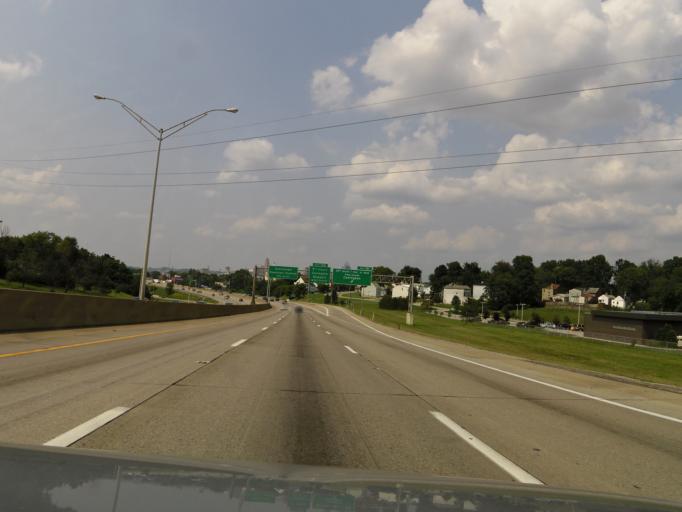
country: US
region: Kentucky
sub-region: Kenton County
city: Park Hills
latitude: 39.0714
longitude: -84.5193
